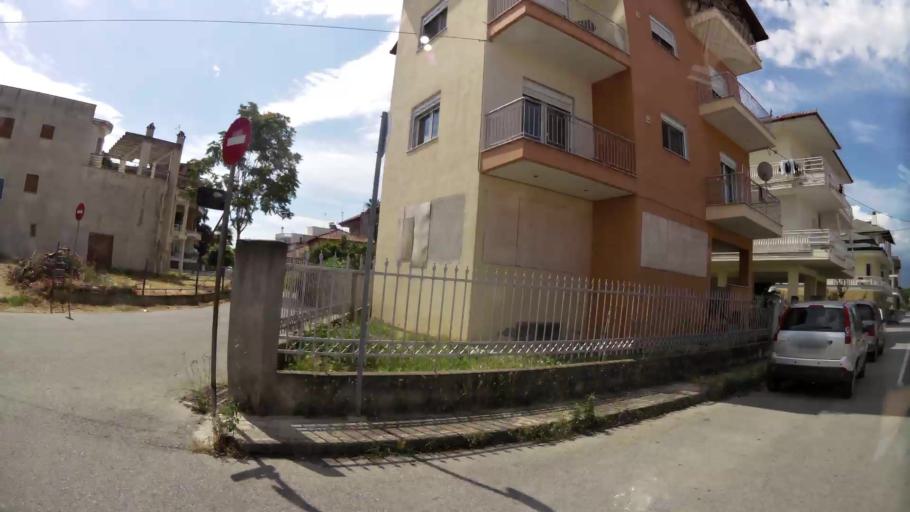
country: GR
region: Central Macedonia
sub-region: Nomos Pierias
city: Katerini
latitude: 40.2684
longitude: 22.4964
